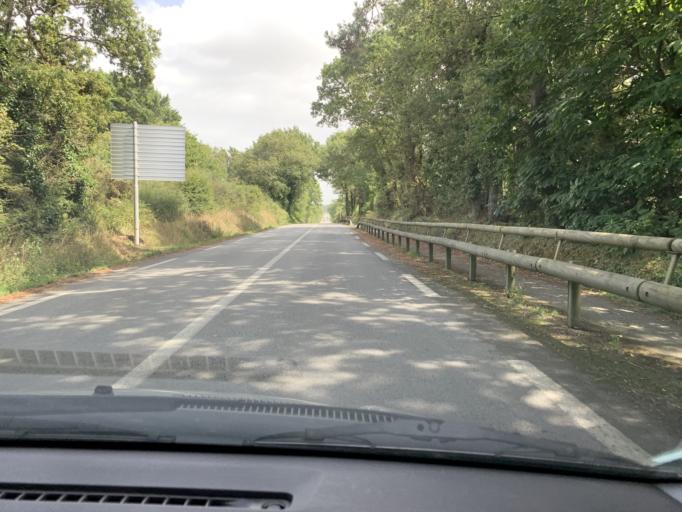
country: FR
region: Brittany
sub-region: Departement du Morbihan
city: Penestin
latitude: 47.4822
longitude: -2.4672
